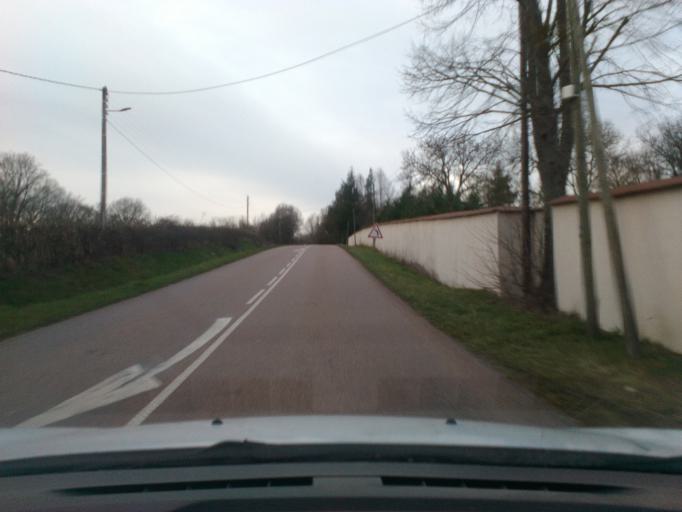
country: FR
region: Lorraine
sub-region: Departement des Vosges
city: Portieux
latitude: 48.3533
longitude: 6.3355
